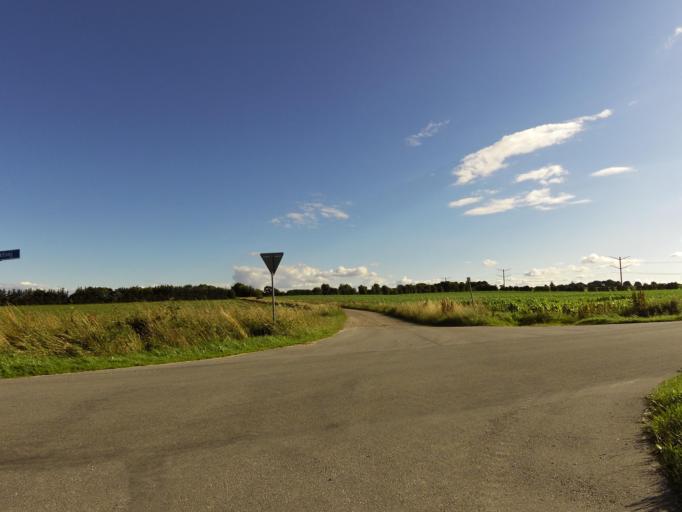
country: DK
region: South Denmark
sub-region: Vejen Kommune
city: Rodding
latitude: 55.3155
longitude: 9.1701
